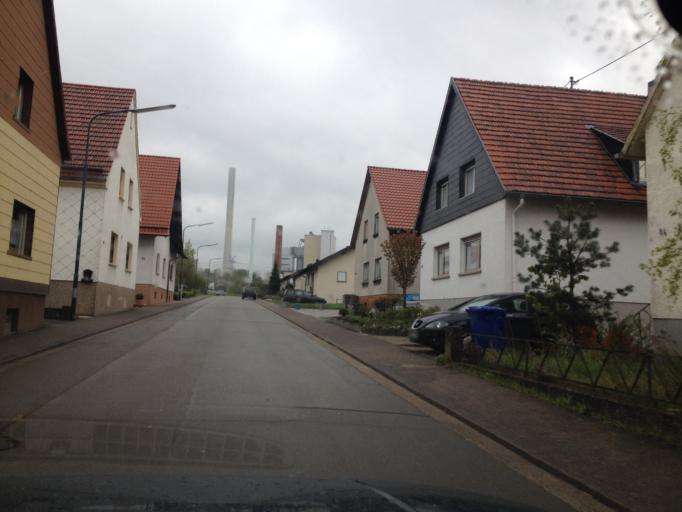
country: DE
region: Saarland
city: Bexbach
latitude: 49.3556
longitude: 7.2298
